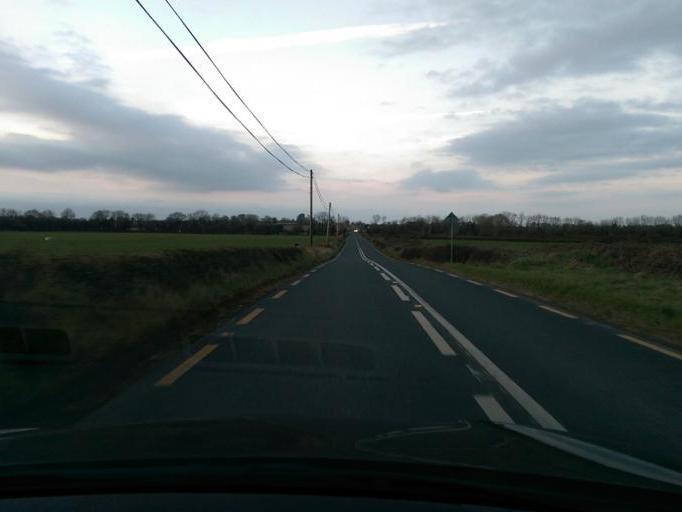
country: IE
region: Connaught
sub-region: County Galway
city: Portumna
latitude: 53.0065
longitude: -8.1255
